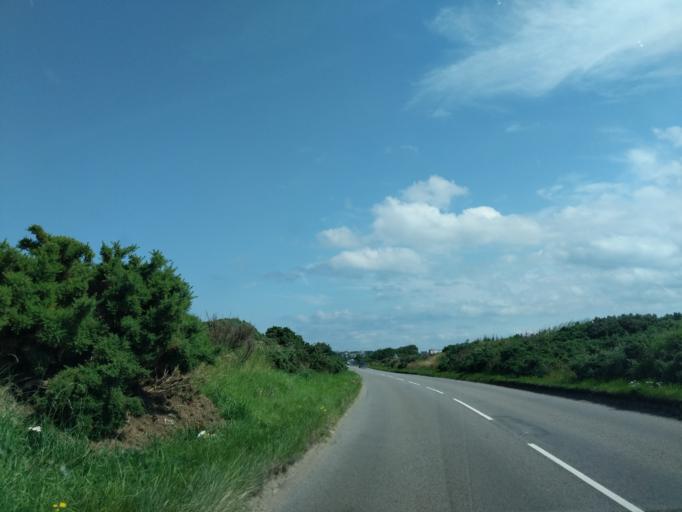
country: GB
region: Scotland
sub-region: Moray
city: Lossiemouth
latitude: 57.7188
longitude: -3.3284
